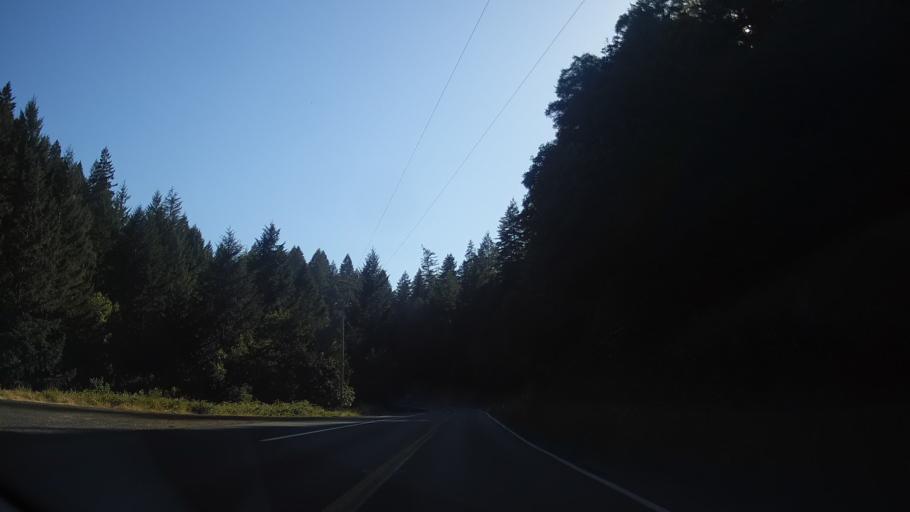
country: US
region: California
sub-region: Mendocino County
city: Brooktrails
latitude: 39.3886
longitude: -123.4324
